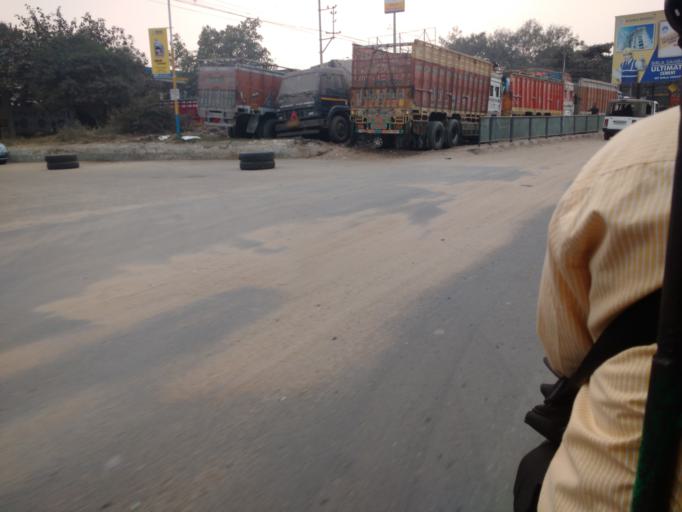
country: IN
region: West Bengal
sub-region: North 24 Parganas
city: Baranagar
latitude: 22.6516
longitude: 88.3659
